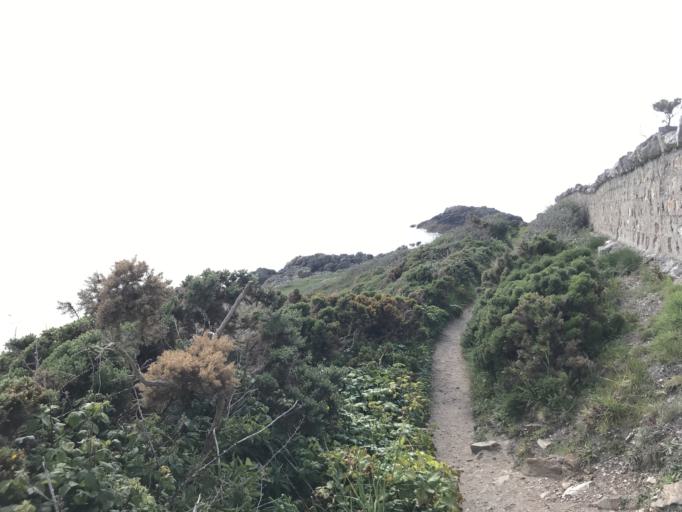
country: IE
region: Leinster
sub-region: Fingal County
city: Howth
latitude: 53.3649
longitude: -6.0866
